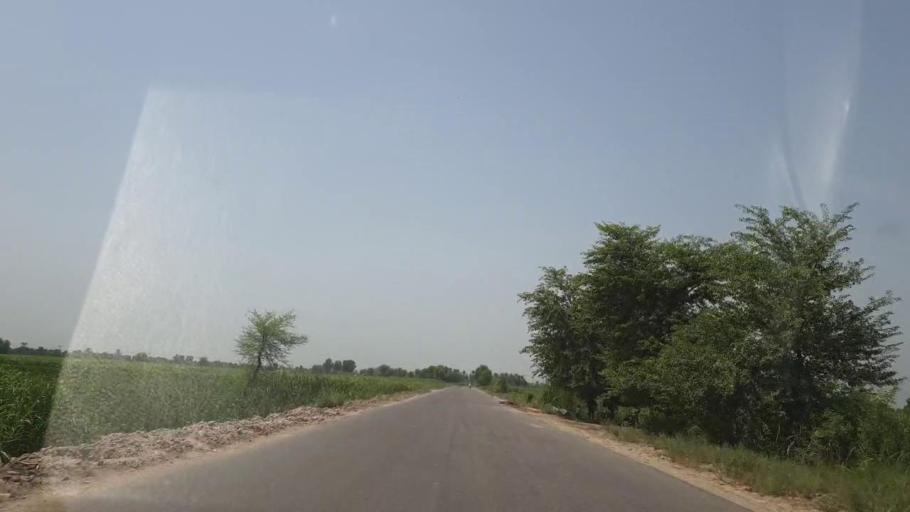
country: PK
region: Sindh
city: Ranipur
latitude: 27.2962
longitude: 68.6049
